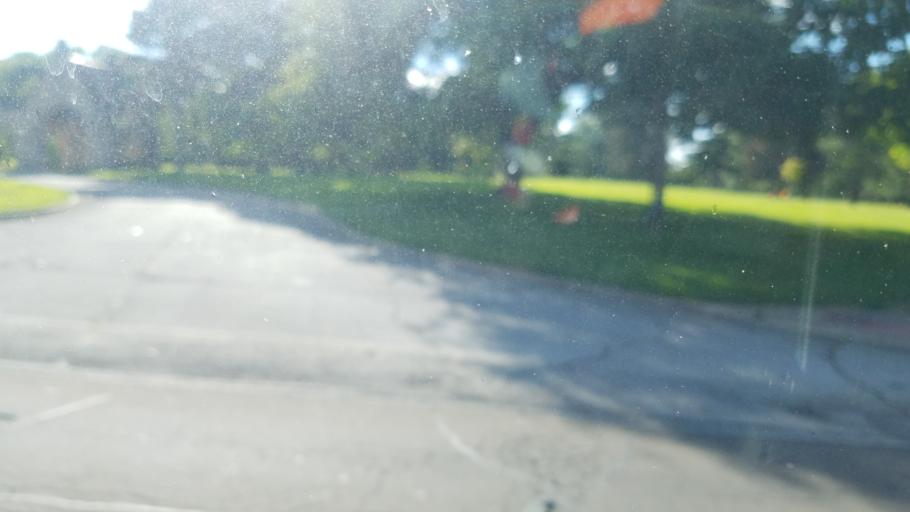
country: US
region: Ohio
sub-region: Mahoning County
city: Boardman
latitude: 41.0436
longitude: -80.6628
